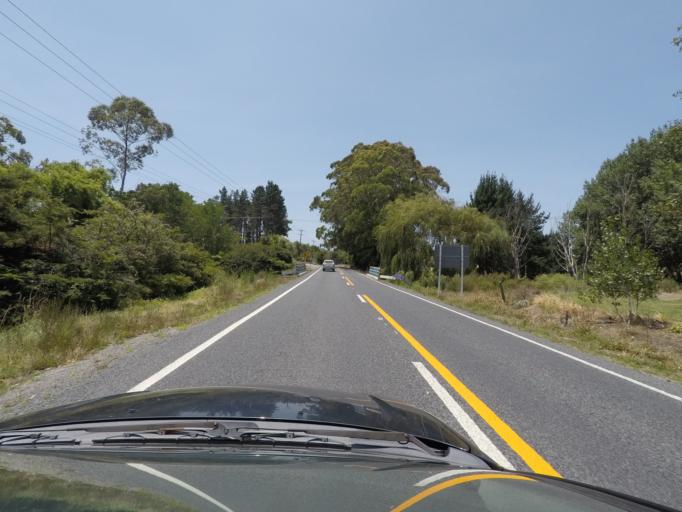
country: NZ
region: Auckland
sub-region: Auckland
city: Warkworth
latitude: -36.3713
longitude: 174.7045
